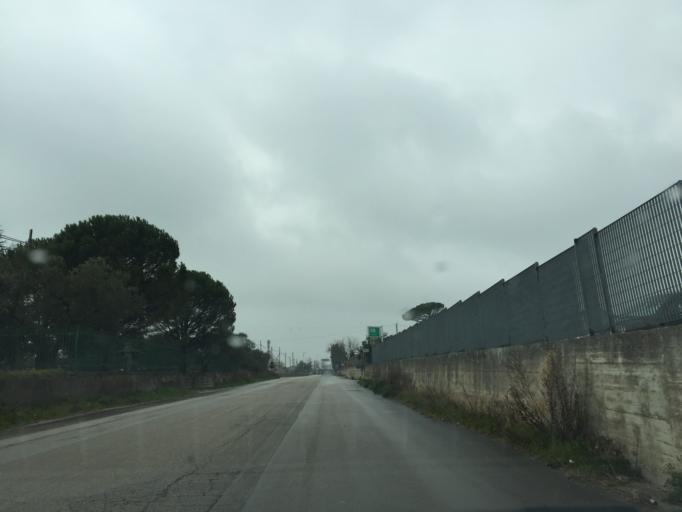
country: IT
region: Apulia
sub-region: Provincia di Foggia
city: Troia
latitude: 41.3684
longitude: 15.3348
